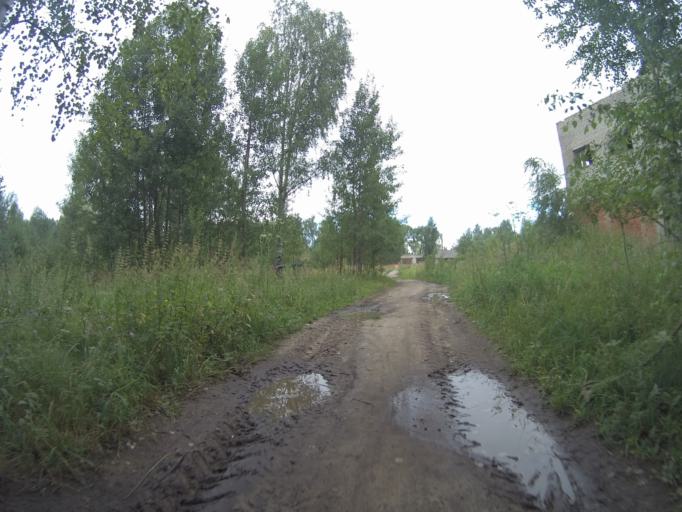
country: RU
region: Vladimir
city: Raduzhnyy
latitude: 55.9958
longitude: 40.2104
